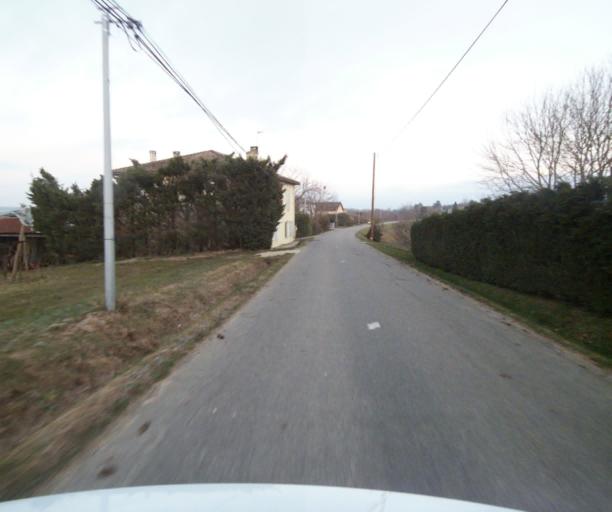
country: FR
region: Midi-Pyrenees
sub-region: Departement du Tarn-et-Garonne
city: Moissac
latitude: 44.1220
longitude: 1.0795
